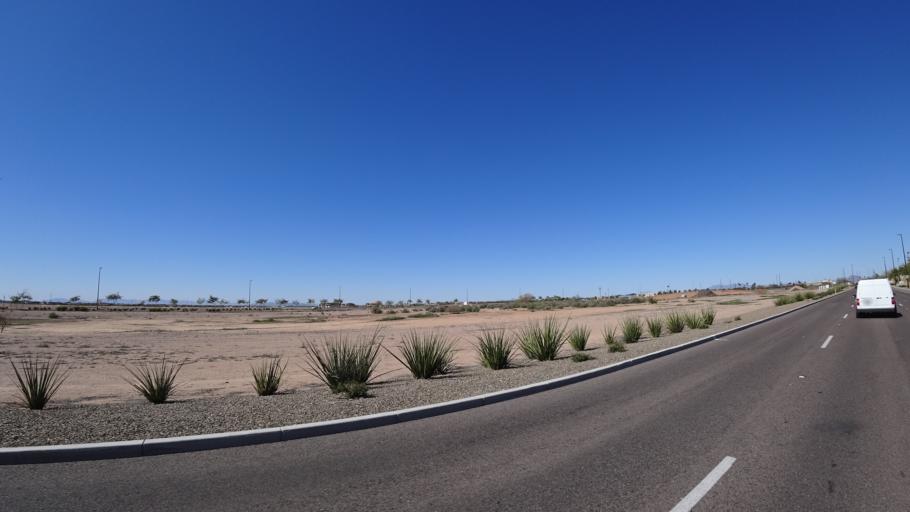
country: US
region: Arizona
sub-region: Maricopa County
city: Queen Creek
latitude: 33.3034
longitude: -111.6867
